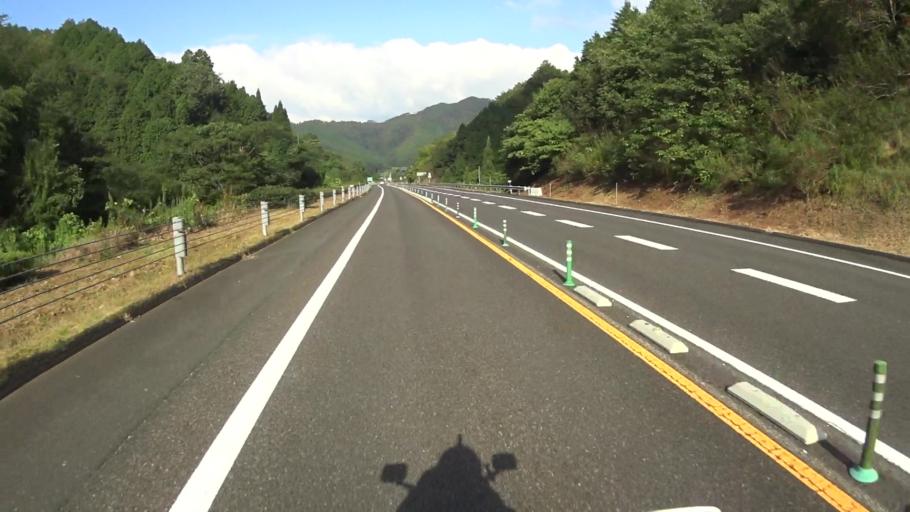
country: JP
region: Kyoto
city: Ayabe
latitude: 35.3825
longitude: 135.2501
